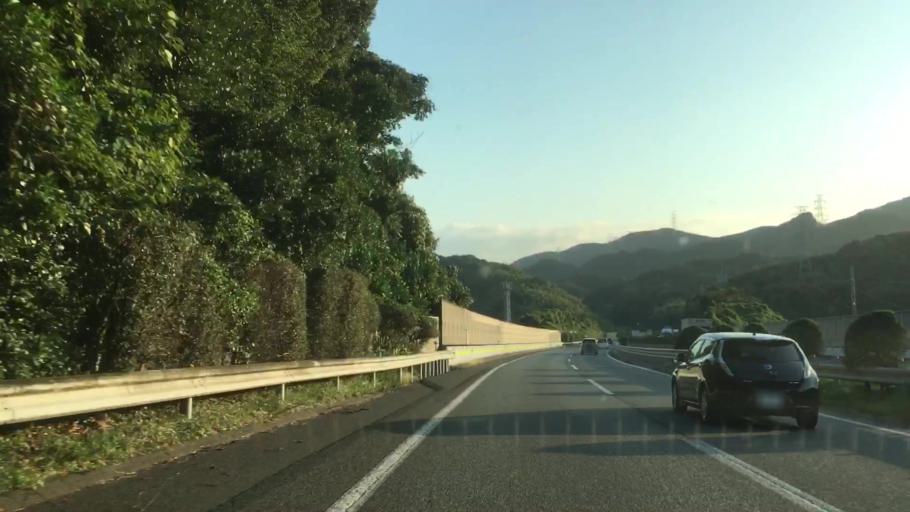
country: JP
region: Yamaguchi
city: Shimonoseki
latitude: 33.9100
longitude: 130.9750
